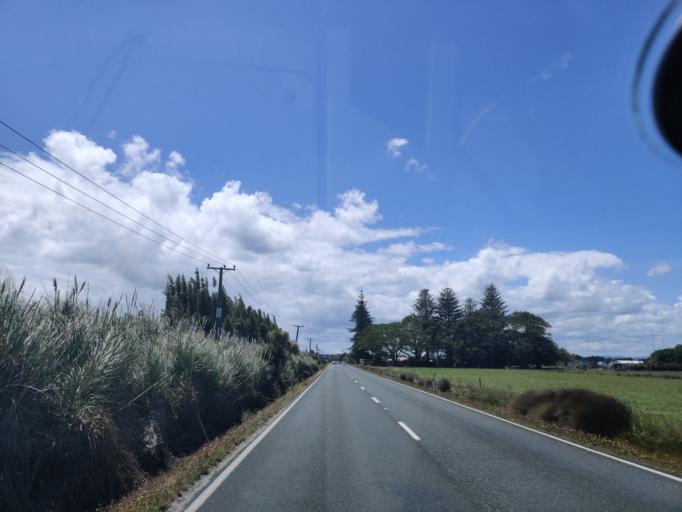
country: NZ
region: Northland
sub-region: Far North District
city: Kaitaia
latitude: -35.0251
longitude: 173.2361
